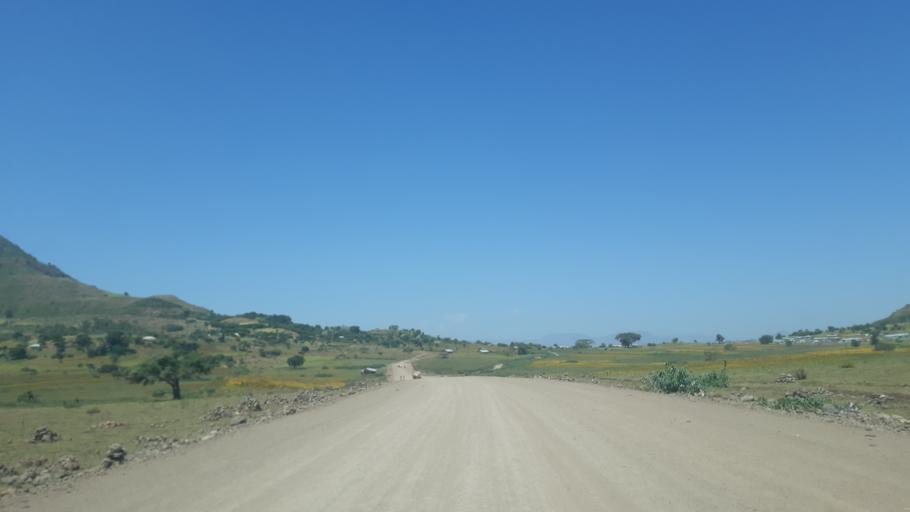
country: ET
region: Amhara
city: Dabat
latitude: 13.1563
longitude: 37.6129
